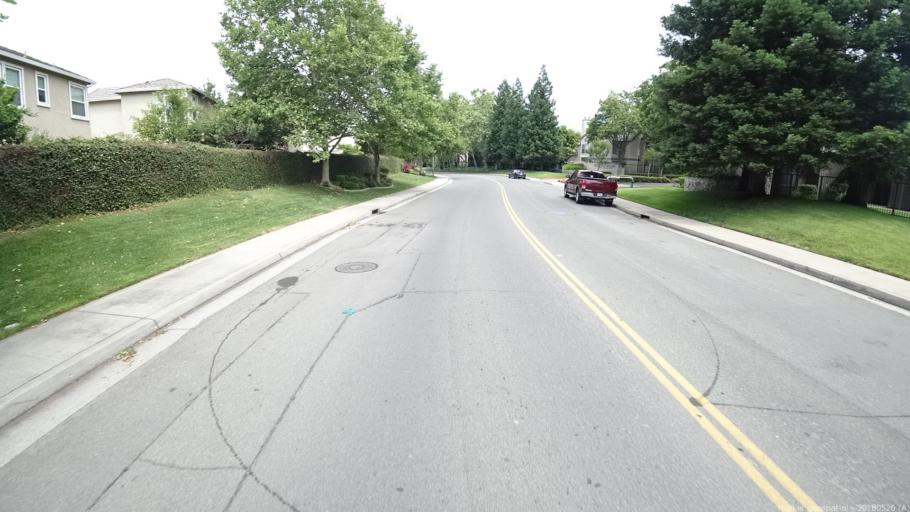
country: US
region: California
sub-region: Yolo County
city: West Sacramento
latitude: 38.6181
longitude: -121.5207
